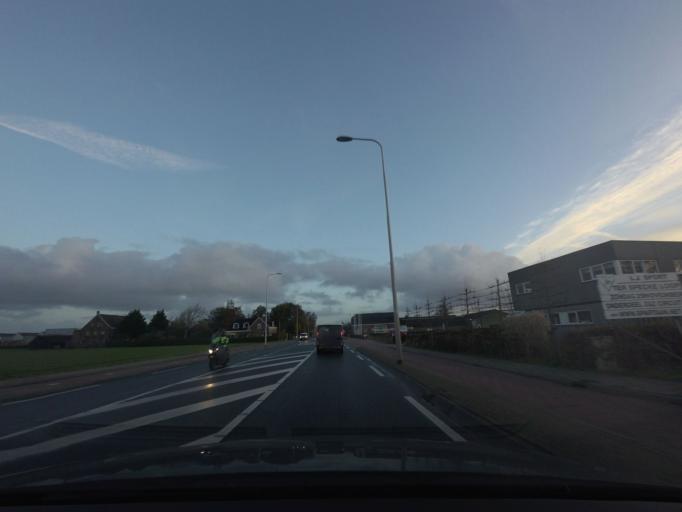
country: NL
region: South Holland
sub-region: Gemeente Teylingen
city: Sassenheim
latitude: 52.2369
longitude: 4.5346
